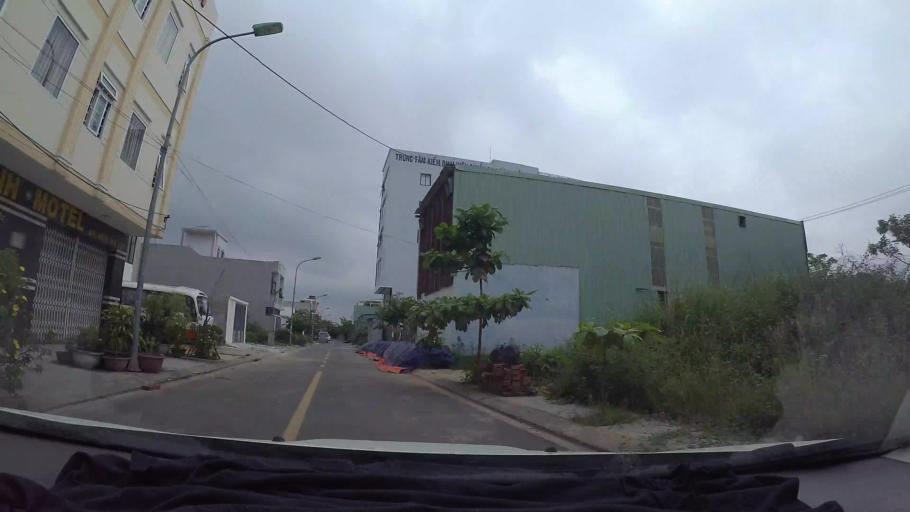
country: VN
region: Da Nang
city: Lien Chieu
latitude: 16.0721
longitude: 108.1641
